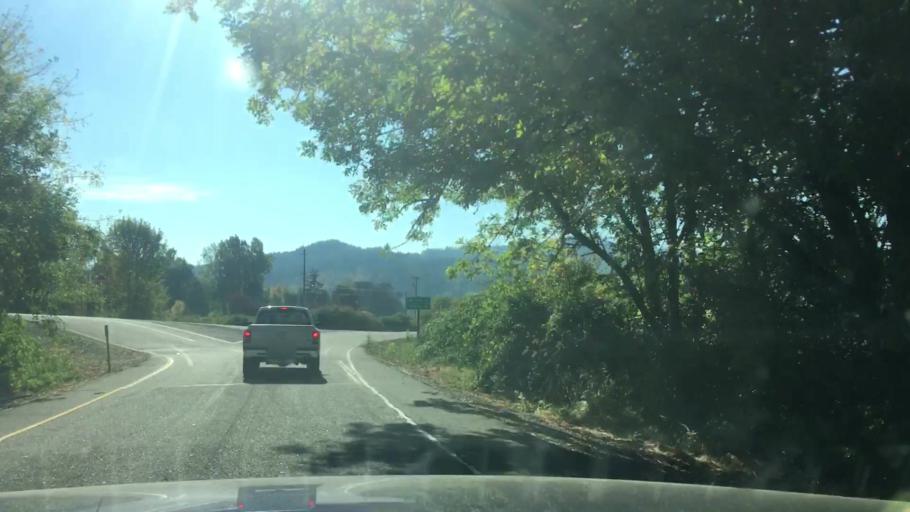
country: US
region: Oregon
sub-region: Lane County
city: Cottage Grove
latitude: 43.8330
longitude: -123.0315
